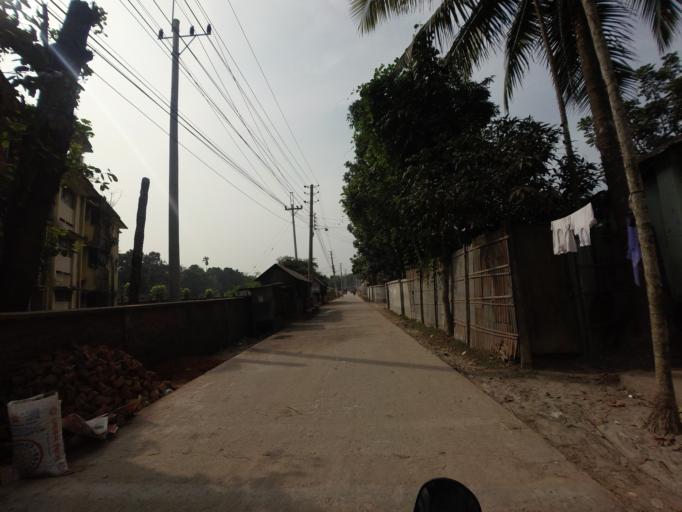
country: BD
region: Rajshahi
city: Saidpur
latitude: 25.9267
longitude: 88.8581
